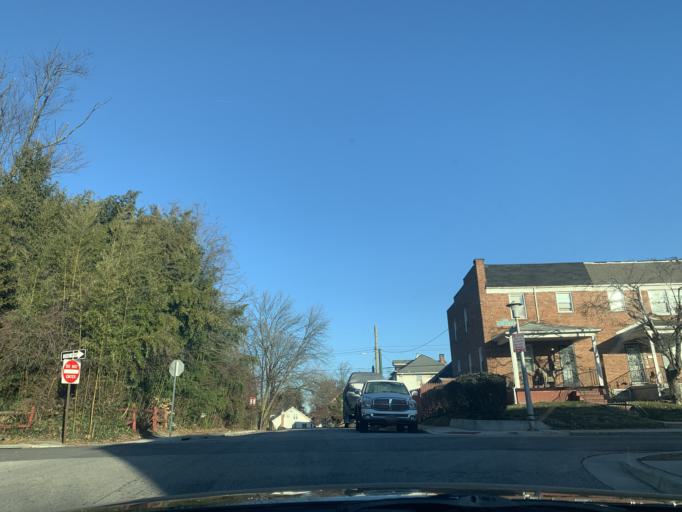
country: US
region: Maryland
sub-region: Baltimore County
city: Lochearn
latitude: 39.3227
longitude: -76.6895
